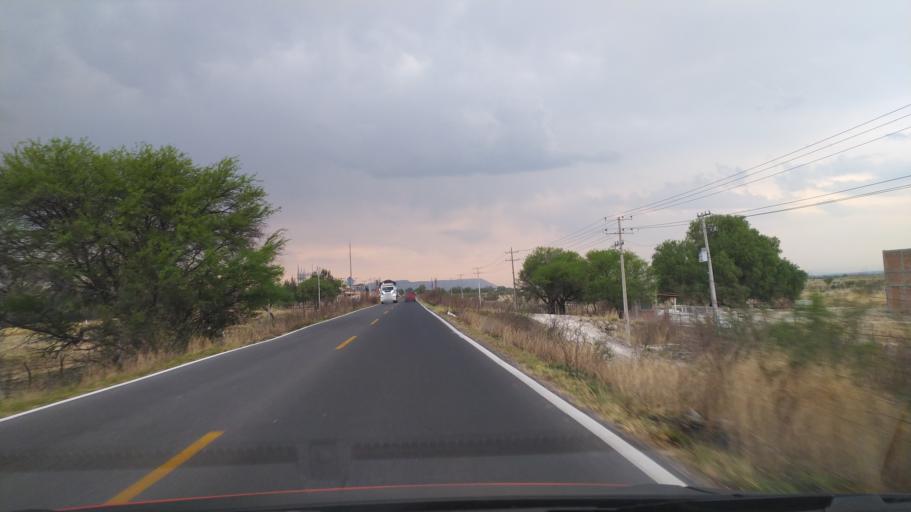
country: MX
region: Guanajuato
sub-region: San Francisco del Rincon
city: San Ignacio de Hidalgo
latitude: 20.8228
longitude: -101.9020
